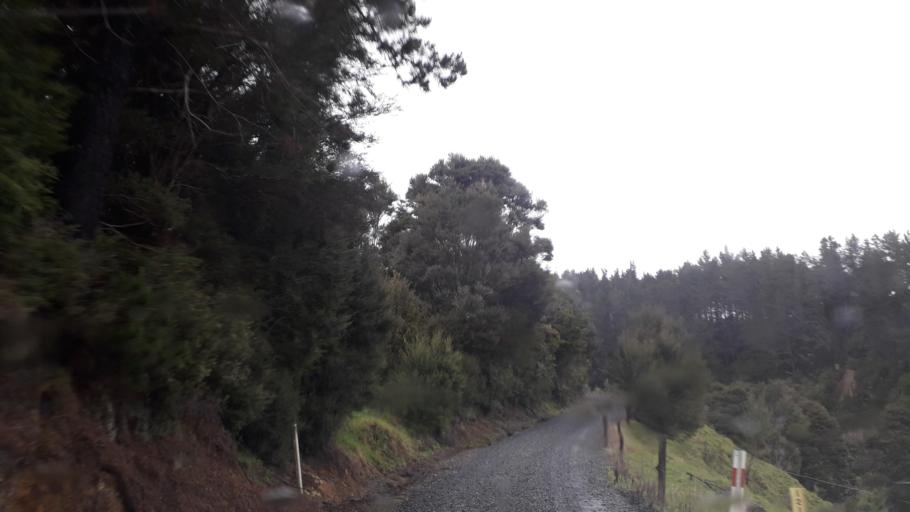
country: NZ
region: Northland
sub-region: Far North District
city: Waimate North
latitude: -35.1582
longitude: 173.7124
